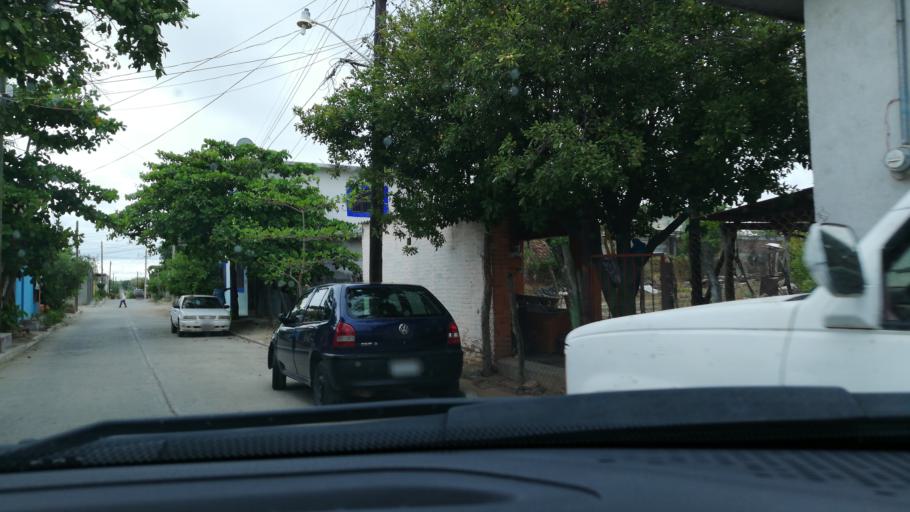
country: MX
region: Oaxaca
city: San Jeronimo Ixtepec
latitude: 16.5652
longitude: -95.1033
